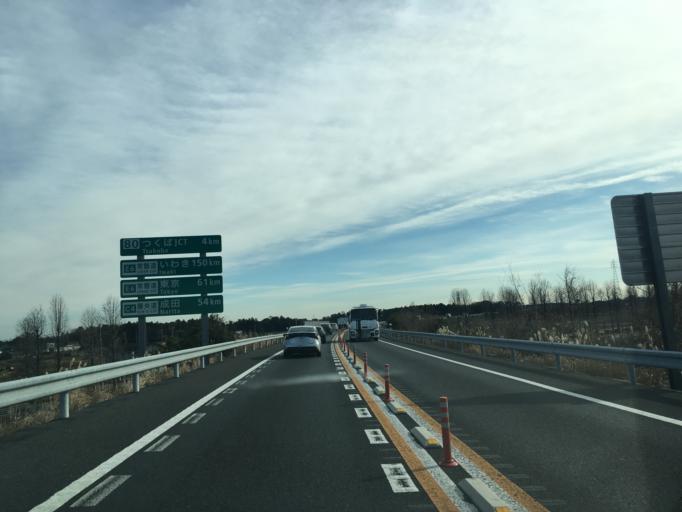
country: JP
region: Ibaraki
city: Naka
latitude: 36.0543
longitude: 140.1003
